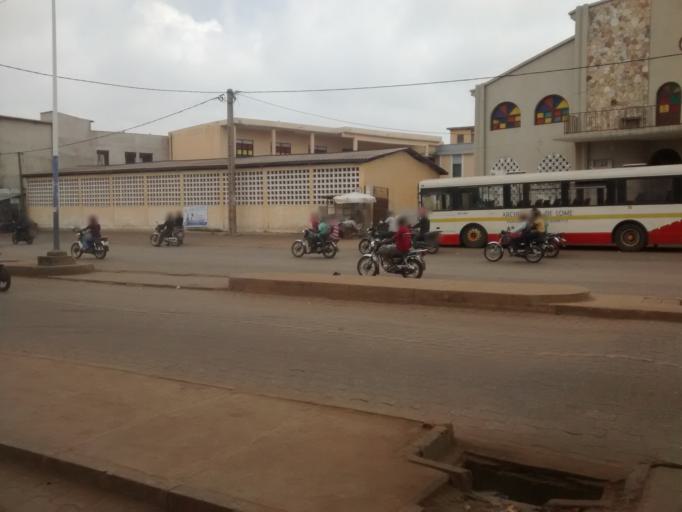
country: TG
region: Maritime
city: Lome
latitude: 6.1581
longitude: 1.2560
